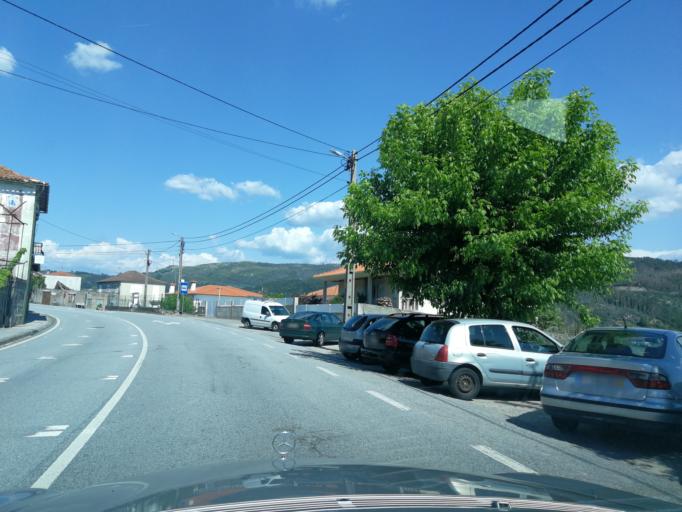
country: PT
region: Braga
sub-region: Braga
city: Adaufe
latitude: 41.5719
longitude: -8.3727
